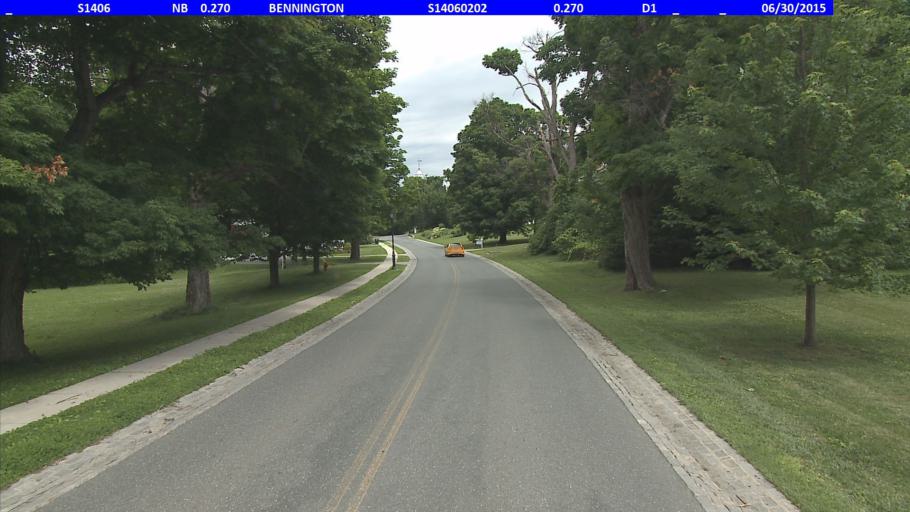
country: US
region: Vermont
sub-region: Bennington County
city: Bennington
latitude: 42.8812
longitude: -73.2125
